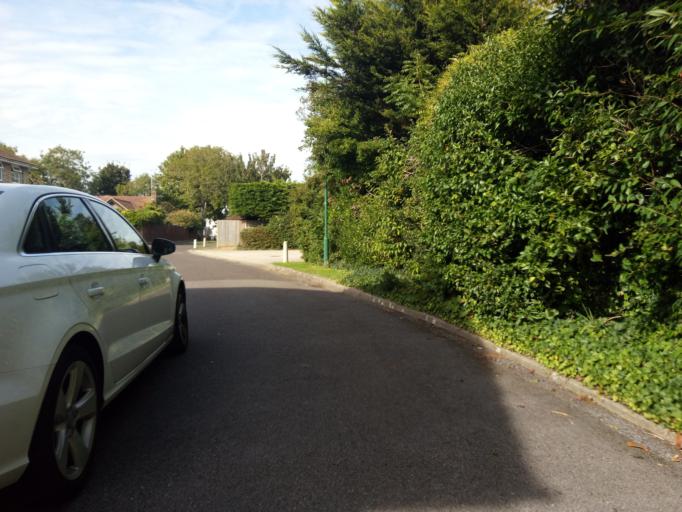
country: GB
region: England
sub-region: West Sussex
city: Barnham
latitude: 50.7945
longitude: -0.6383
